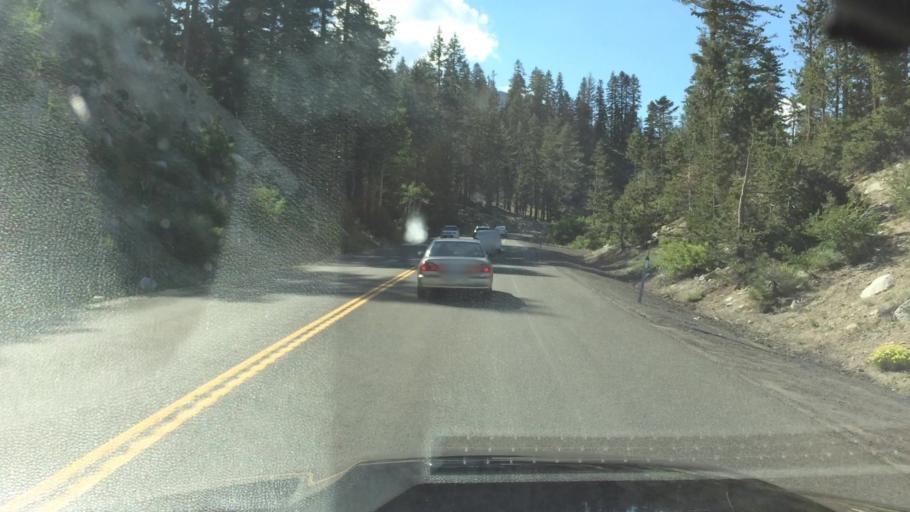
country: US
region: Nevada
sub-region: Washoe County
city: Incline Village
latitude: 39.3264
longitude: -119.8777
